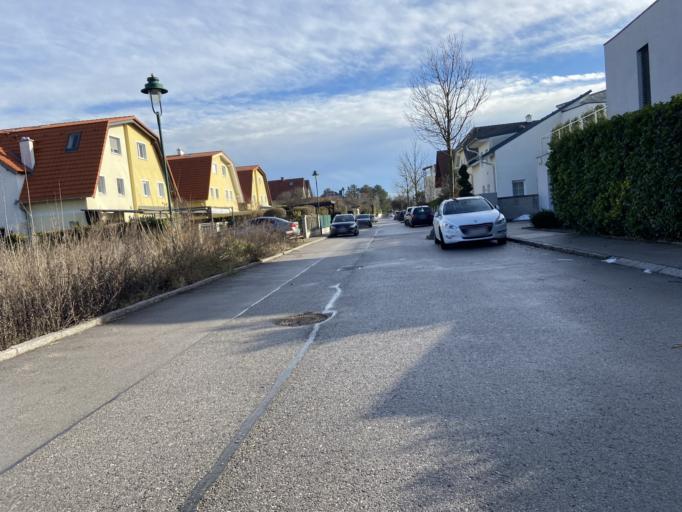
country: AT
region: Lower Austria
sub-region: Politischer Bezirk Modling
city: Laxenburg
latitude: 48.0733
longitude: 16.3499
